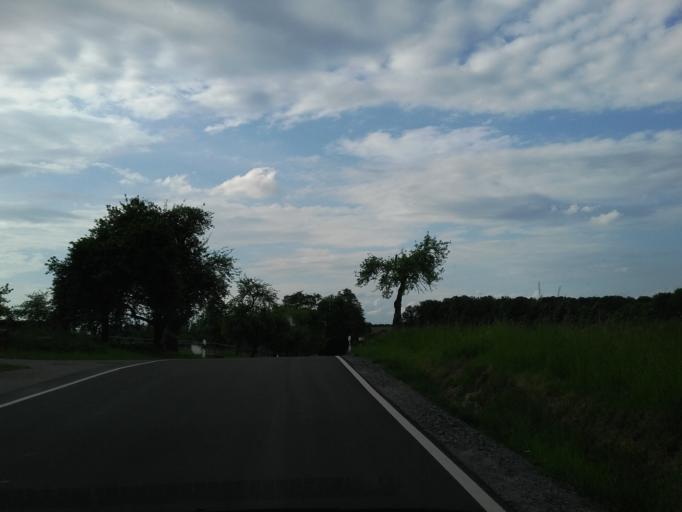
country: DE
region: Baden-Wuerttemberg
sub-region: Regierungsbezirk Stuttgart
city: Oberstenfeld
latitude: 49.0009
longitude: 9.3462
